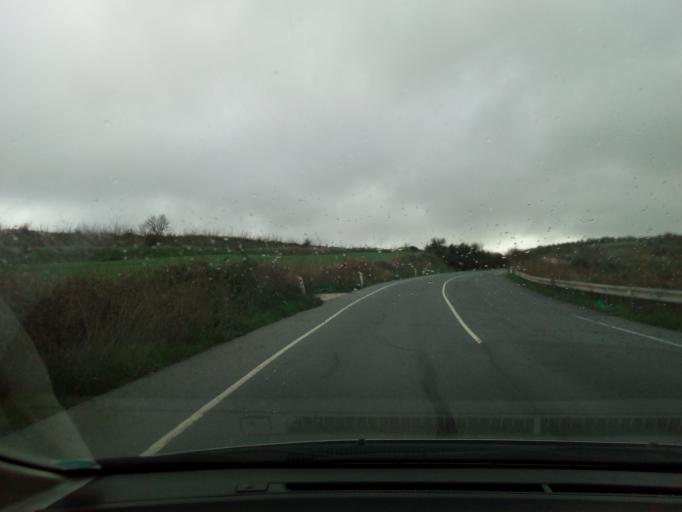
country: CY
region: Pafos
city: Tala
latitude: 34.9048
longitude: 32.4683
